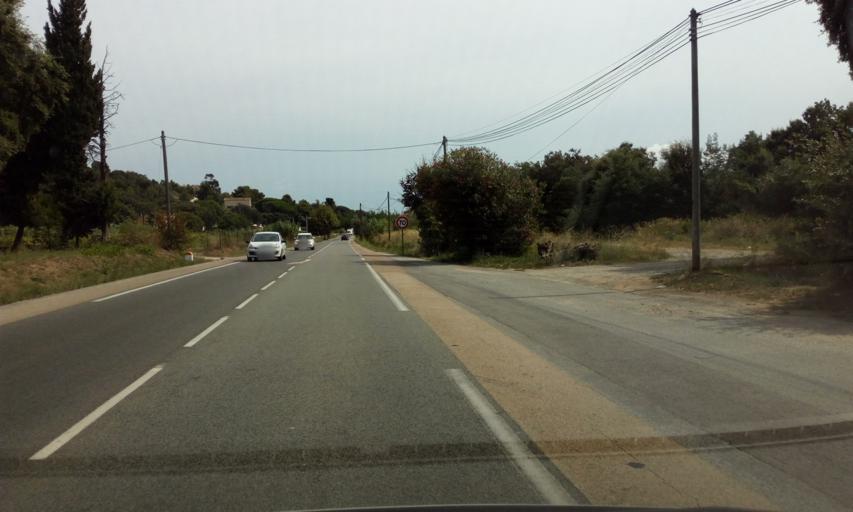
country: FR
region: Provence-Alpes-Cote d'Azur
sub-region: Departement du Var
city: Bormes-les-Mimosas
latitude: 43.1504
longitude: 6.3163
